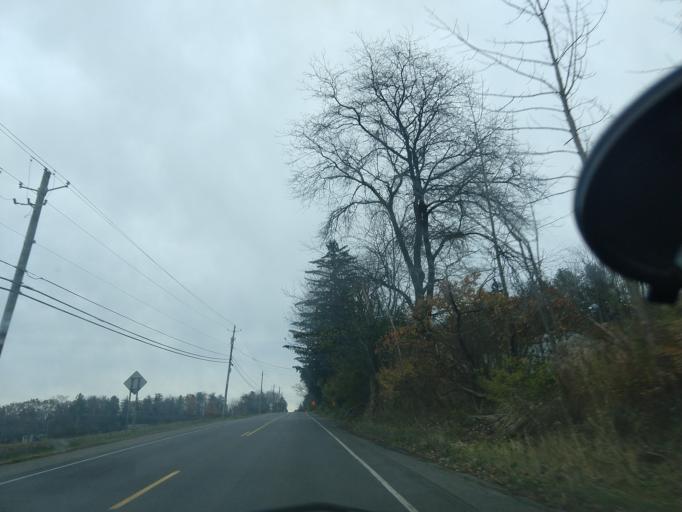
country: US
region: New York
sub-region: Tompkins County
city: East Ithaca
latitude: 42.4338
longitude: -76.4521
